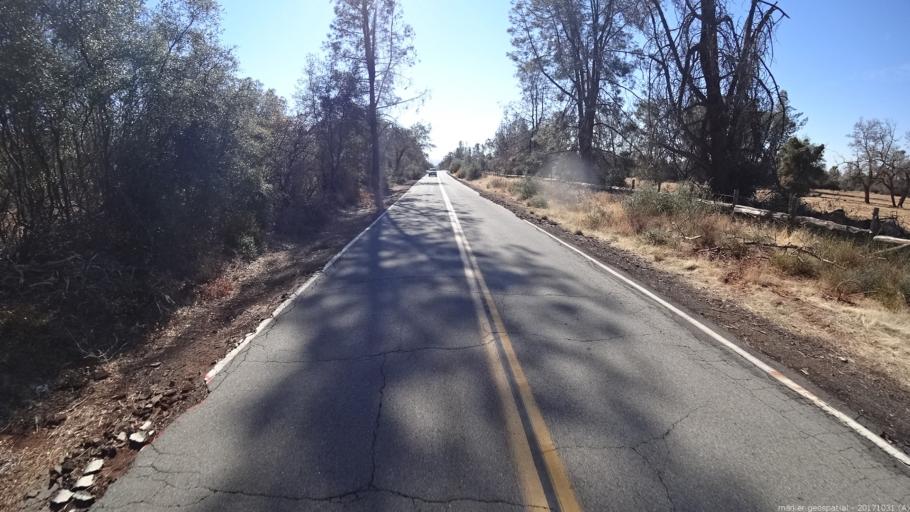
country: US
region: California
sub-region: Shasta County
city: Shingletown
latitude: 40.4480
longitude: -121.8994
